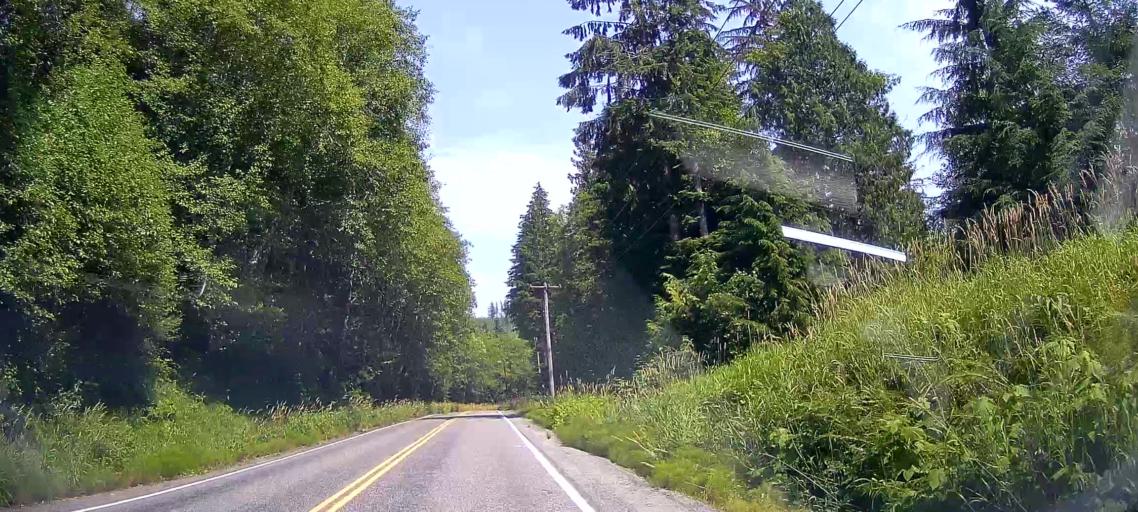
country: US
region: Washington
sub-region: Snohomish County
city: Arlington Heights
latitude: 48.3436
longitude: -122.0602
